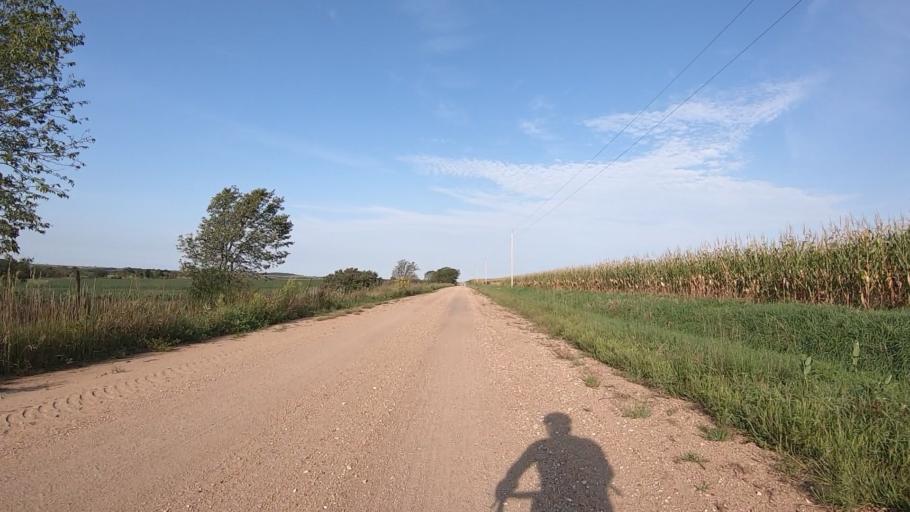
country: US
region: Kansas
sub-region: Marshall County
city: Blue Rapids
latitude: 39.6533
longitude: -96.8450
